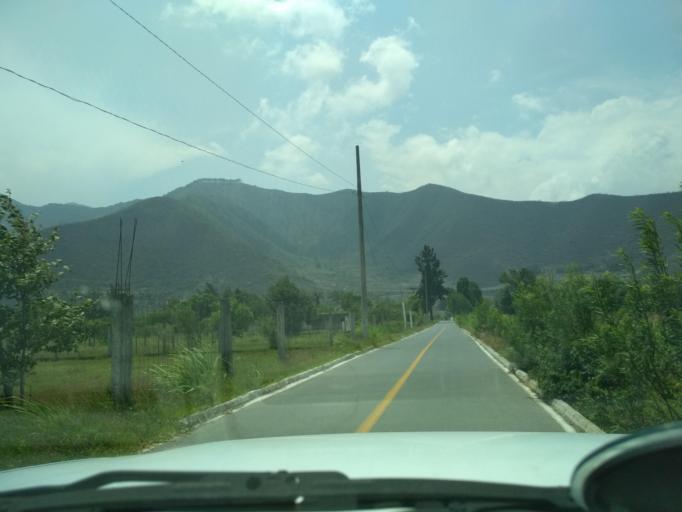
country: MX
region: Veracruz
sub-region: Nogales
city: Taza de Agua Ojo Zarco
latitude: 18.7738
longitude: -97.2165
